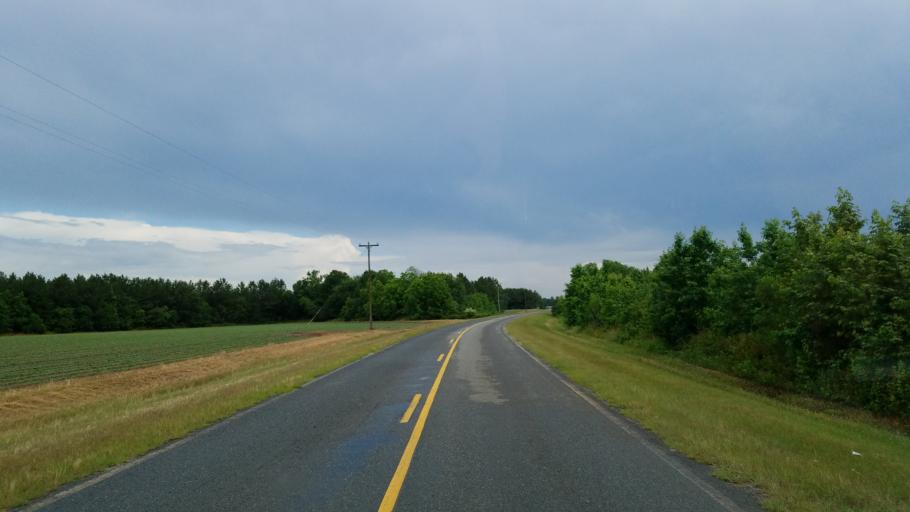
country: US
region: Georgia
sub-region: Dooly County
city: Unadilla
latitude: 32.2195
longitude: -83.7961
